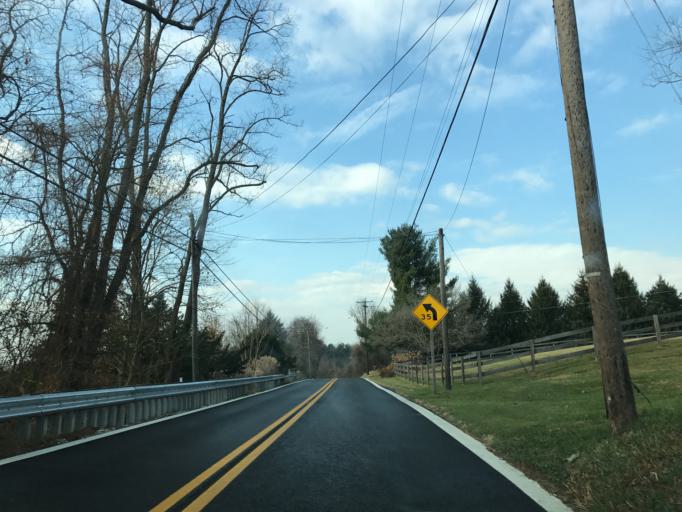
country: US
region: Maryland
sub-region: Baltimore County
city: Hunt Valley
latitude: 39.5857
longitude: -76.5913
